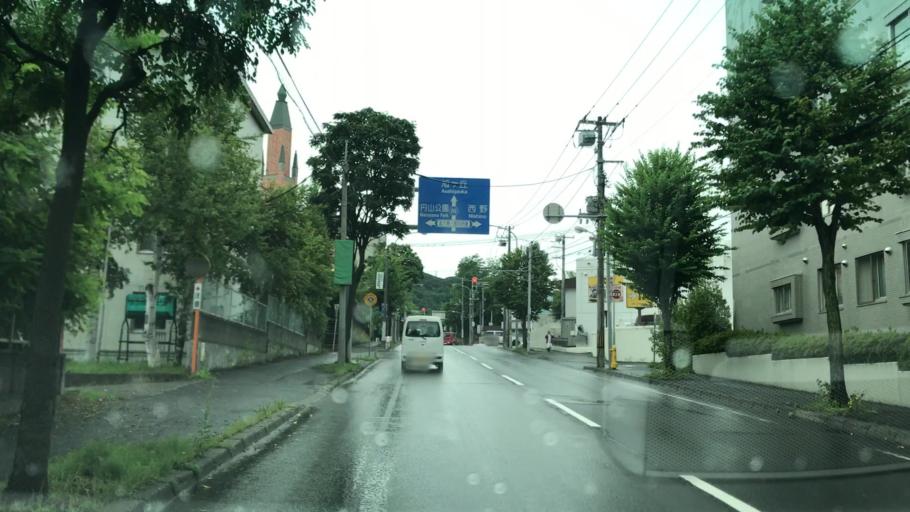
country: JP
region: Hokkaido
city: Sapporo
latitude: 43.0597
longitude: 141.3002
